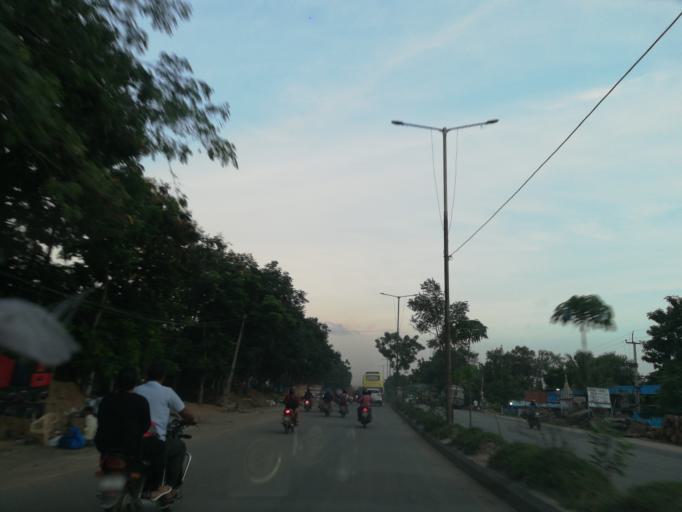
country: IN
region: Telangana
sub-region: Medak
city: Serilingampalle
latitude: 17.5177
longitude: 78.3567
